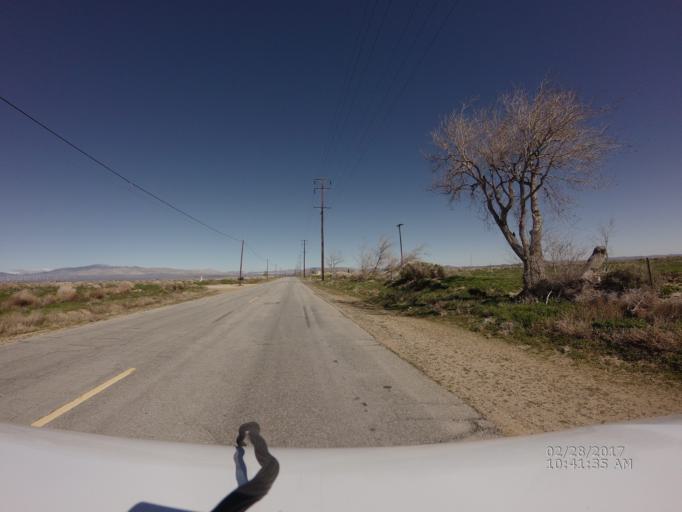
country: US
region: California
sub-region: Kern County
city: Rosamond
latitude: 34.7978
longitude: -118.2903
